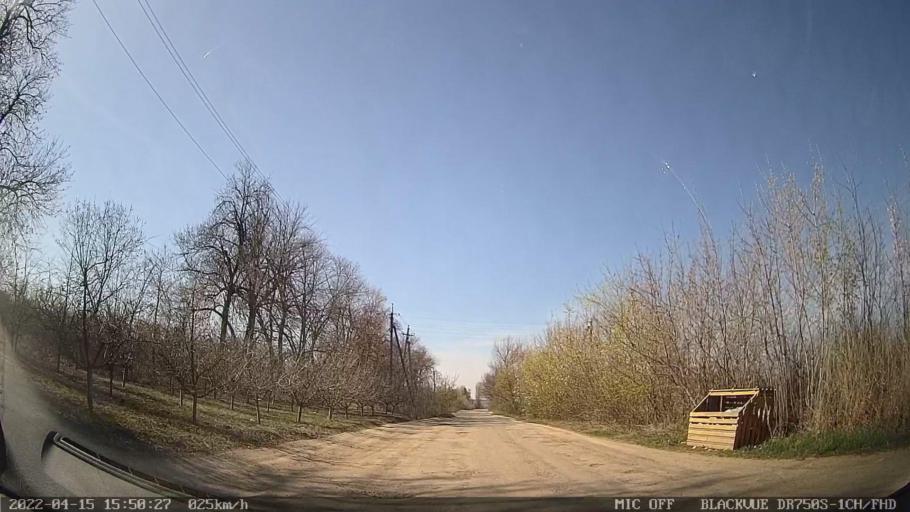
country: MD
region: Raionul Ocnita
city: Otaci
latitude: 48.3918
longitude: 27.9011
